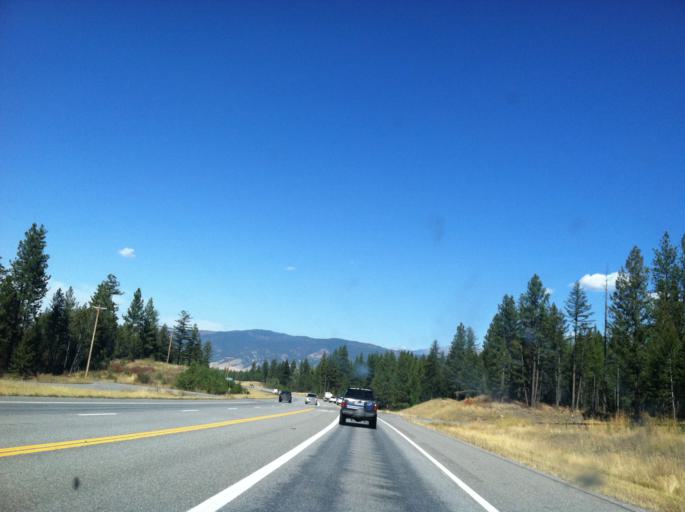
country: US
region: Montana
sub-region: Missoula County
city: Frenchtown
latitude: 47.0877
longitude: -114.0412
